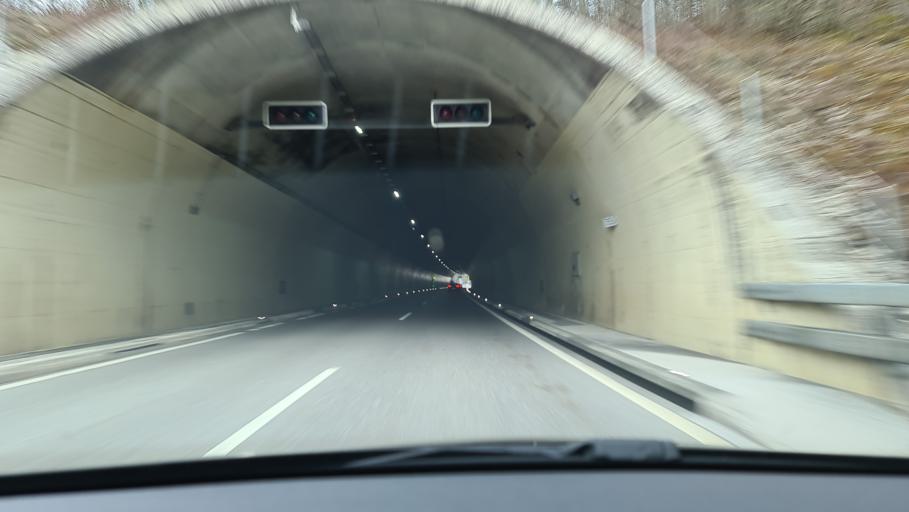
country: CH
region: Bern
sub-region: Jura bernois
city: Orvin
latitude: 47.1875
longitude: 7.2204
